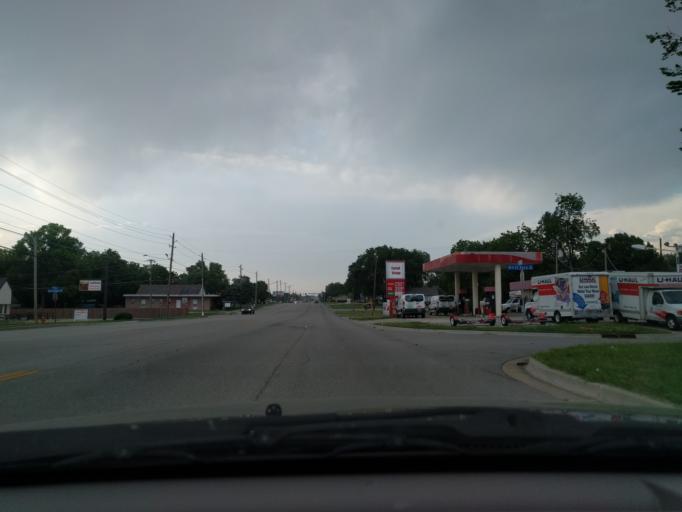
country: US
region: Oklahoma
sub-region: Tulsa County
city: Broken Arrow
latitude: 36.0492
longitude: -95.7974
